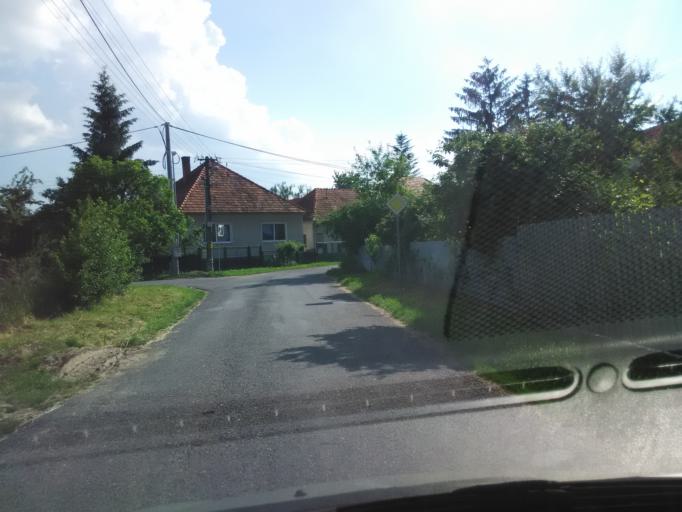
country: SK
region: Nitriansky
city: Tlmace
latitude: 48.3158
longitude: 18.5221
